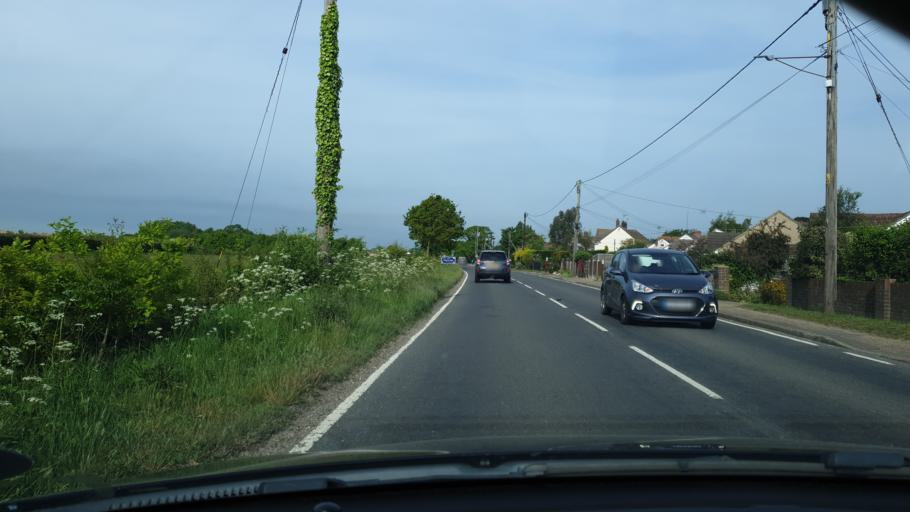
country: GB
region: England
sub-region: Essex
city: Little Clacton
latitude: 51.8544
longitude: 1.1776
